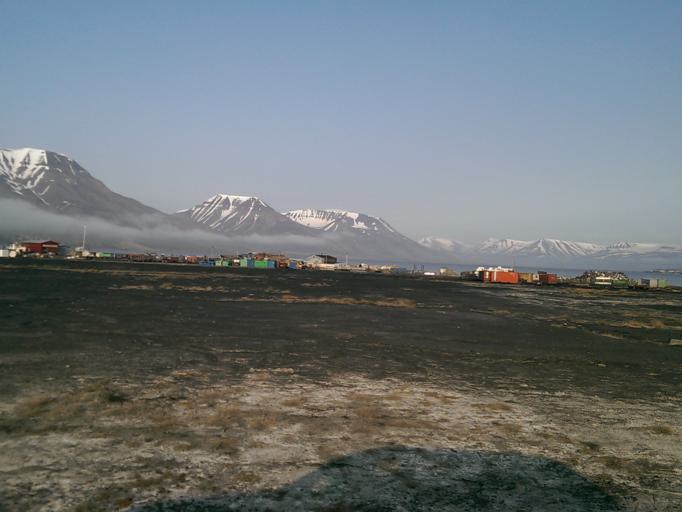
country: SJ
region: Svalbard
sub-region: Spitsbergen
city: Longyearbyen
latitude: 78.2458
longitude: 15.5337
